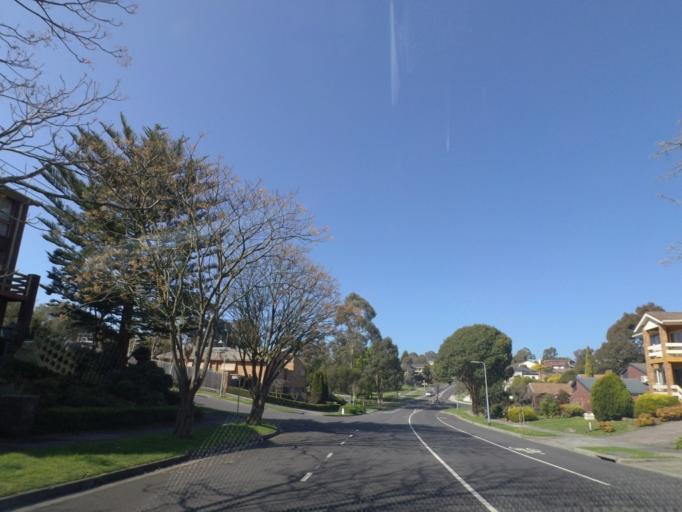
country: AU
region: Victoria
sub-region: Manningham
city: Doncaster East
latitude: -37.7674
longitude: 145.1610
